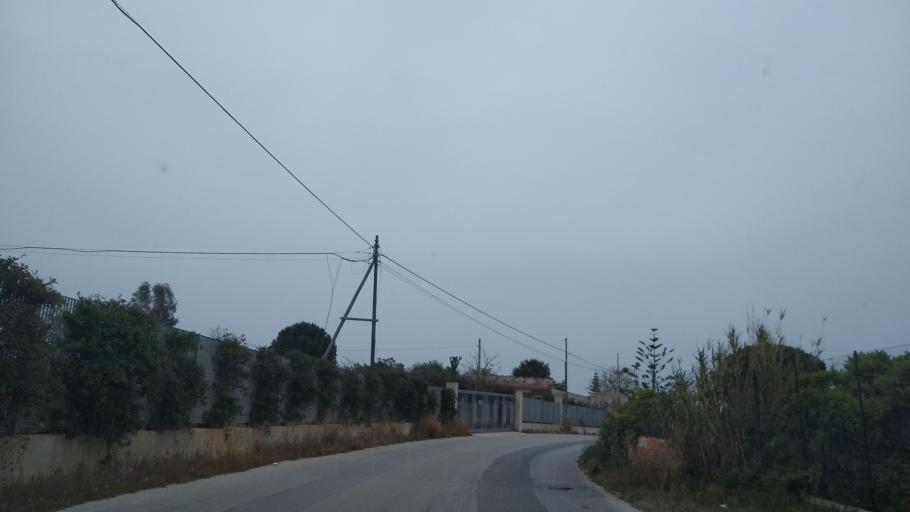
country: IT
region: Sicily
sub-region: Trapani
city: Castellammare del Golfo
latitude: 38.0174
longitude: 12.8959
